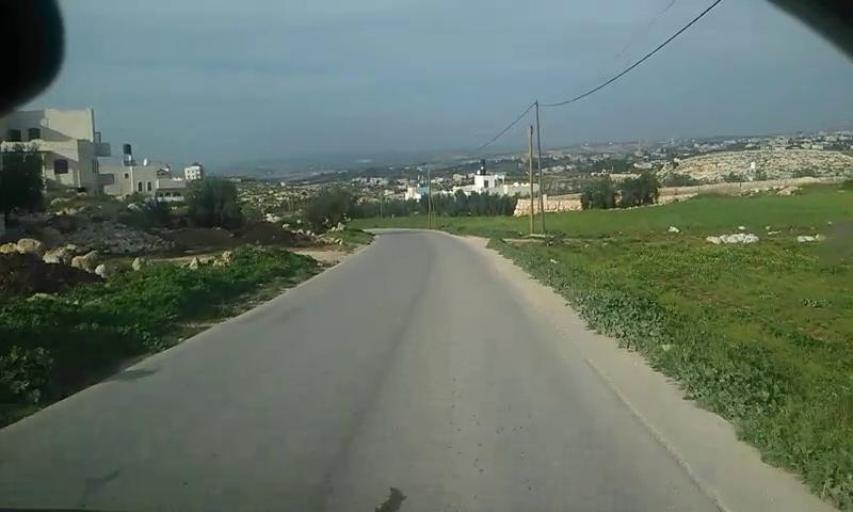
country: PS
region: West Bank
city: Nuba
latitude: 31.6089
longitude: 35.0160
